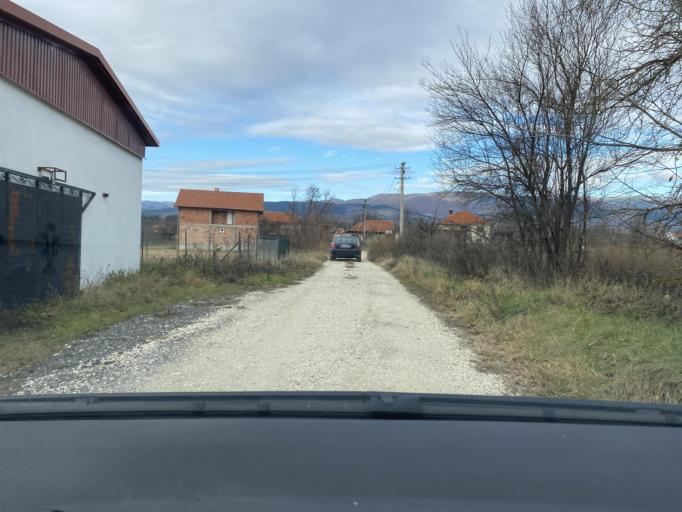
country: MK
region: Opstina Rankovce
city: Rankovce
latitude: 42.1677
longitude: 22.1574
